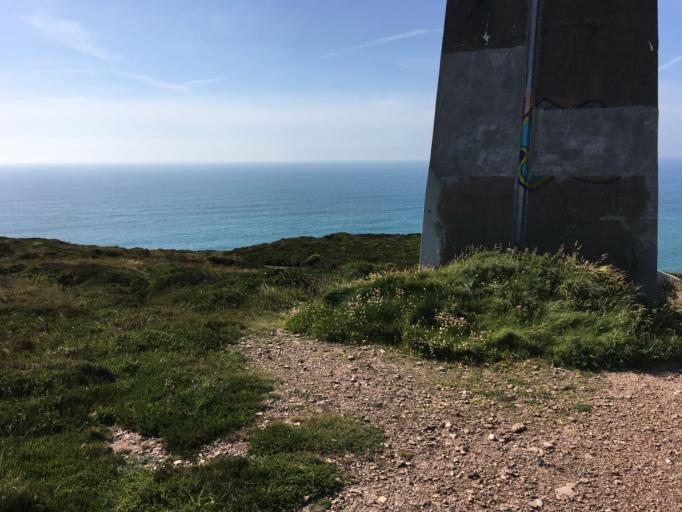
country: GB
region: England
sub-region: Cornwall
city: Redruth
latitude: 50.2798
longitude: -5.2564
